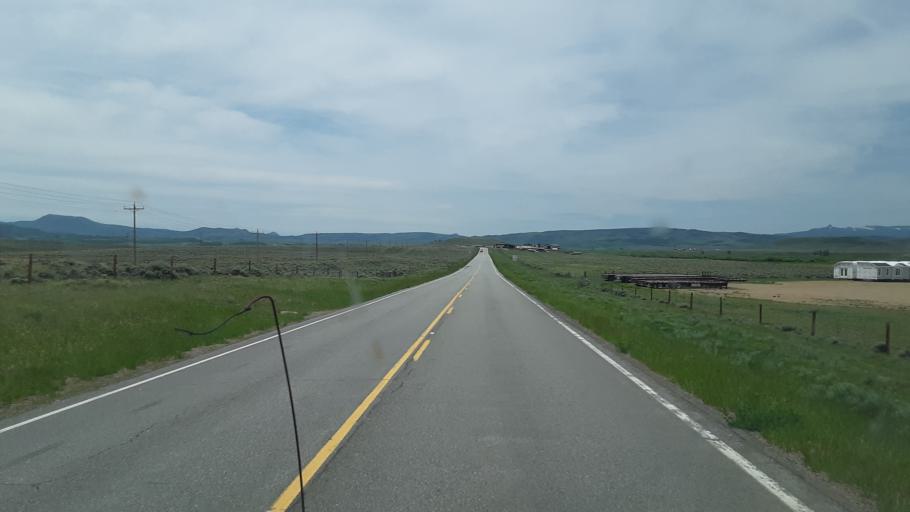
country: US
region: Colorado
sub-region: Jackson County
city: Walden
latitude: 40.5242
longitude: -106.4112
